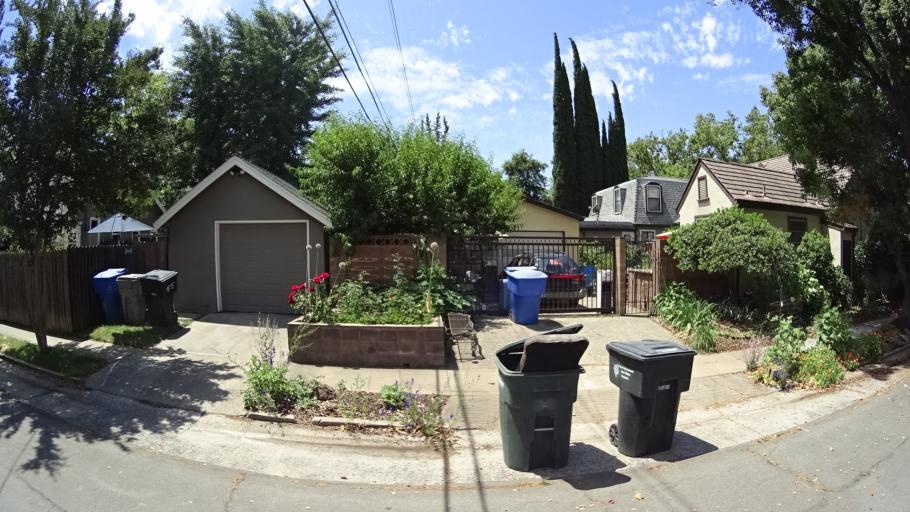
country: US
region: California
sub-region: Sacramento County
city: Sacramento
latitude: 38.5740
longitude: -121.4517
